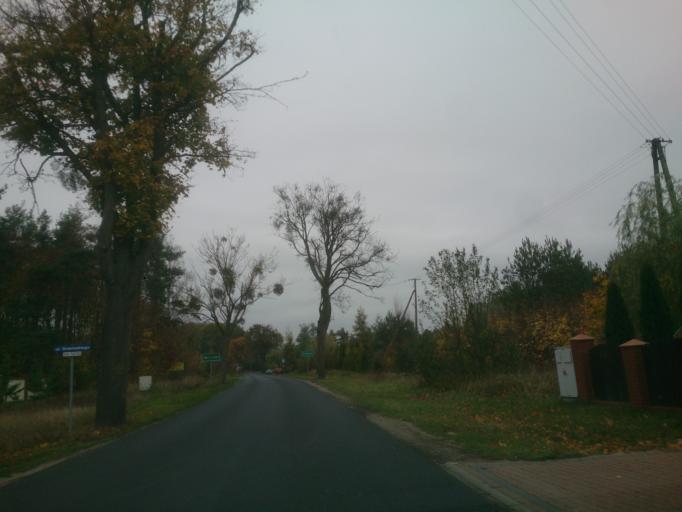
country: PL
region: Kujawsko-Pomorskie
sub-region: Powiat brodnicki
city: Brodnica
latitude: 53.2847
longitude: 19.3870
